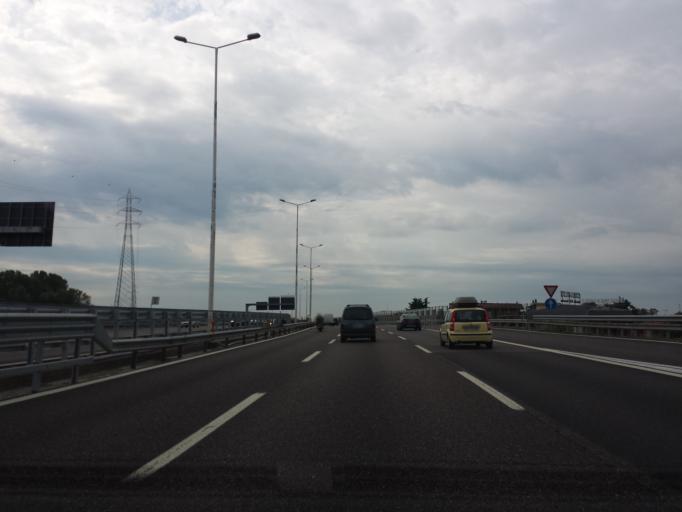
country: IT
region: Lombardy
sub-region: Citta metropolitana di Milano
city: Figino
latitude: 45.4894
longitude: 9.0666
